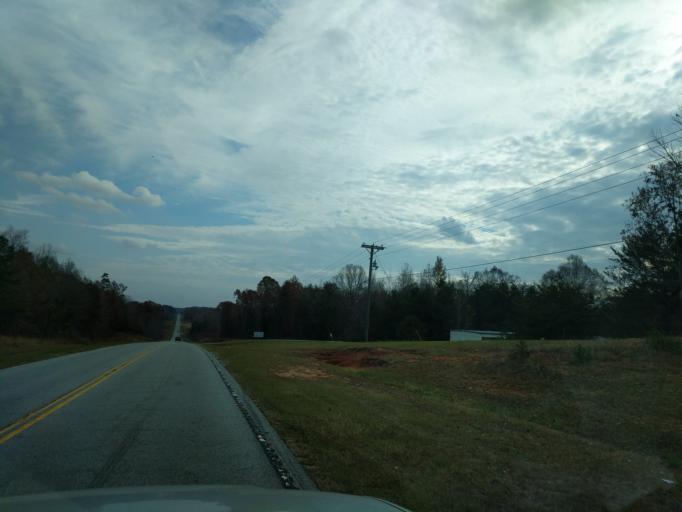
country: US
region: Georgia
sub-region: Franklin County
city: Gumlog
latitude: 34.5277
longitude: -83.0522
